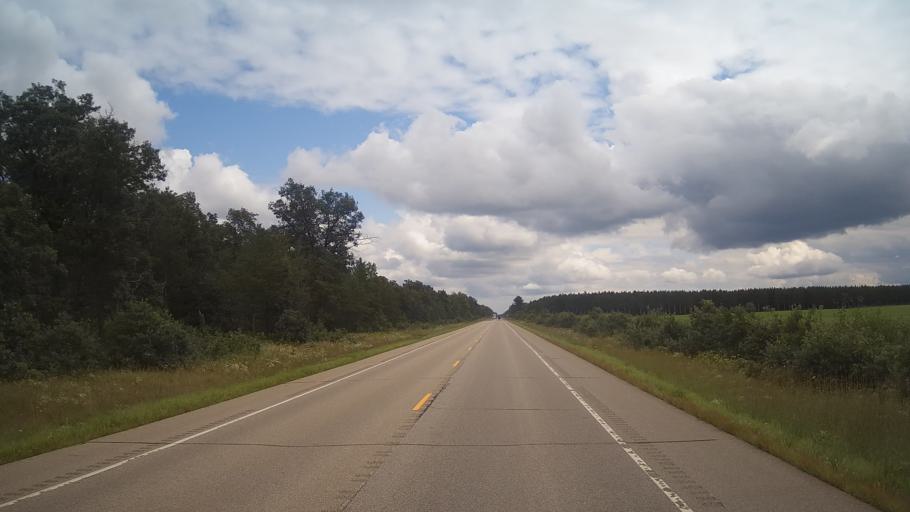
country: US
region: Wisconsin
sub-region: Adams County
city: Friendship
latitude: 44.0250
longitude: -89.7577
